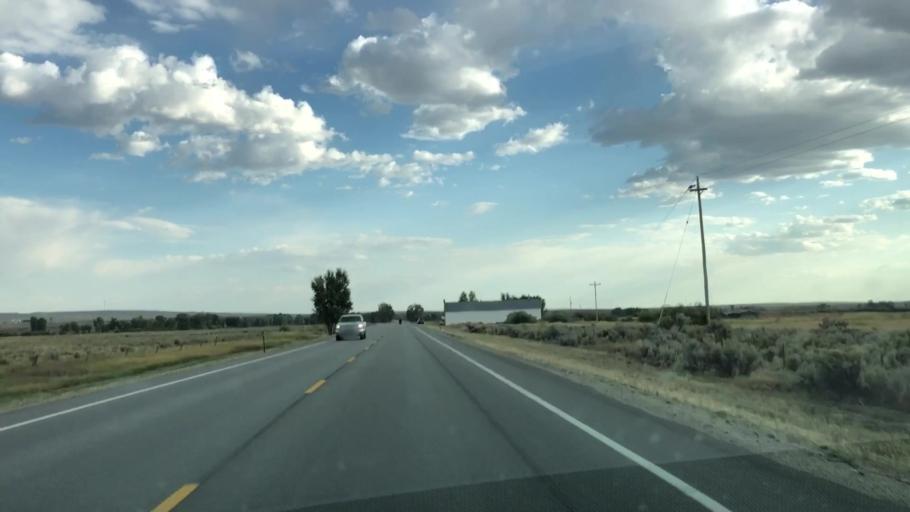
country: US
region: Wyoming
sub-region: Sublette County
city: Pinedale
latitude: 42.7062
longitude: -109.7137
